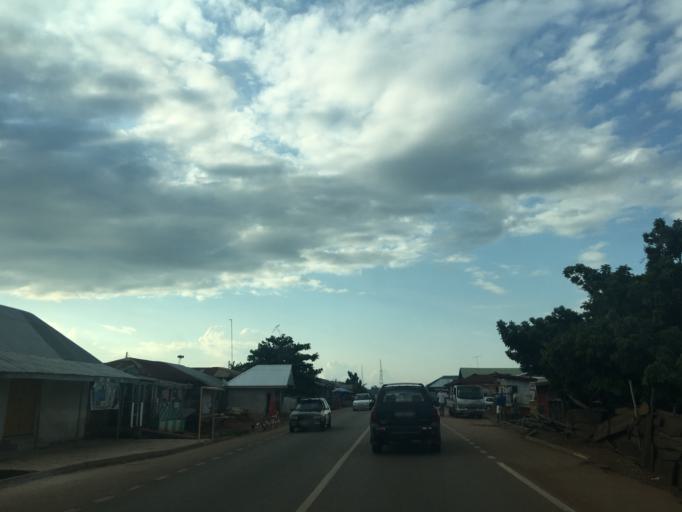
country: GH
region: Western
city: Bibiani
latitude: 6.4446
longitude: -2.3142
